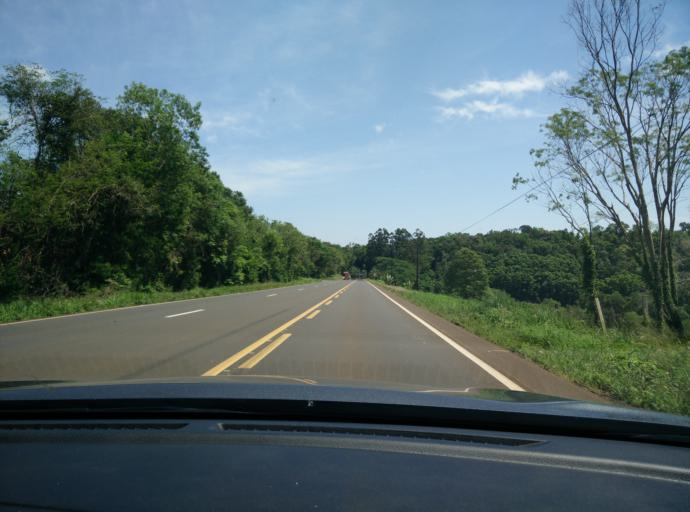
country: BR
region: Parana
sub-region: Santo Antonio Do Sudoeste
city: Santo Antonio do Sudoeste
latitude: -25.8530
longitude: -53.7459
